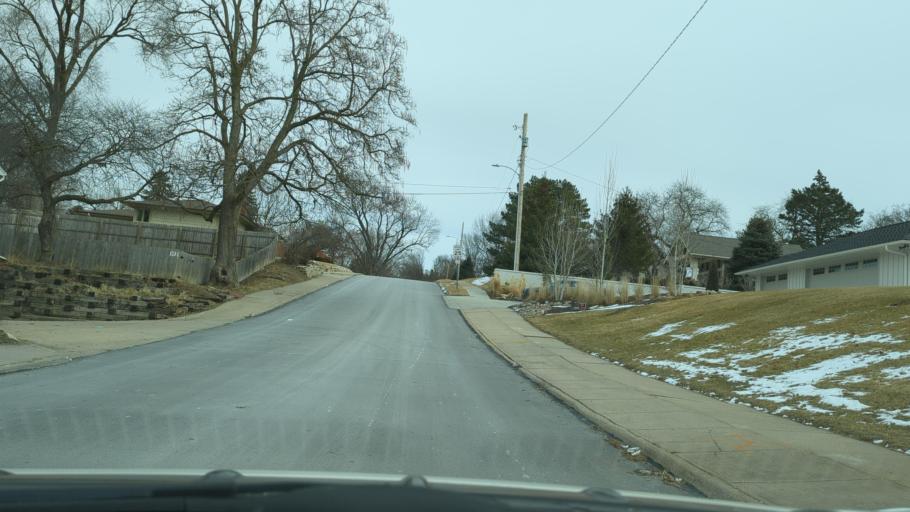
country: US
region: Nebraska
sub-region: Douglas County
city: Ralston
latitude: 41.2669
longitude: -96.0191
